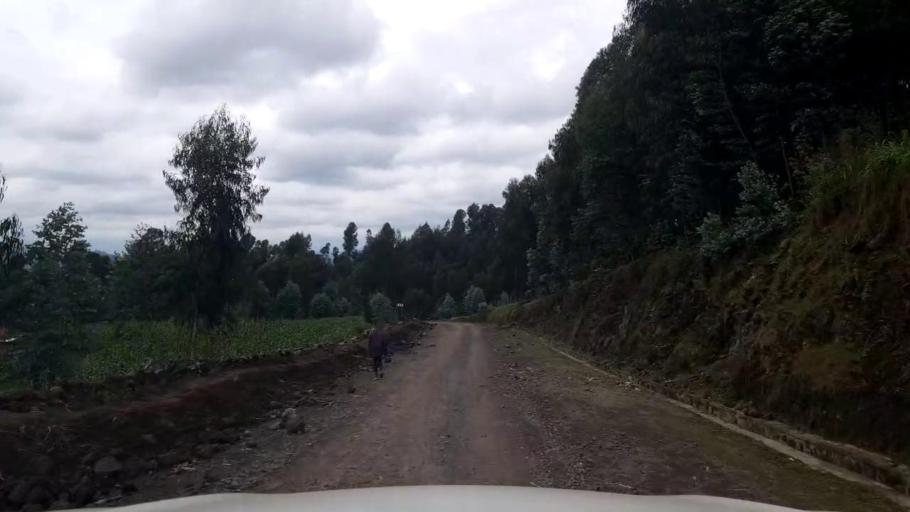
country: RW
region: Northern Province
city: Musanze
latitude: -1.5376
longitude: 29.5331
